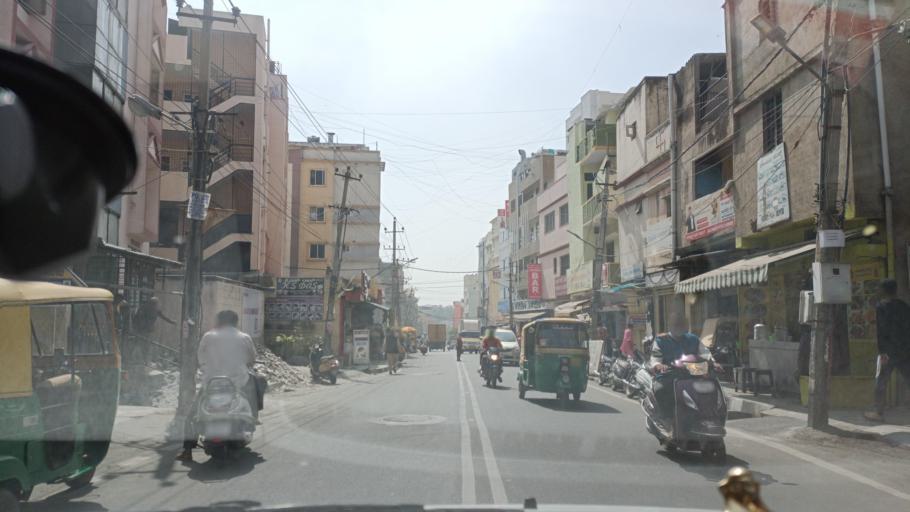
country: IN
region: Karnataka
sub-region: Bangalore Urban
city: Bangalore
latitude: 12.9286
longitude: 77.6093
